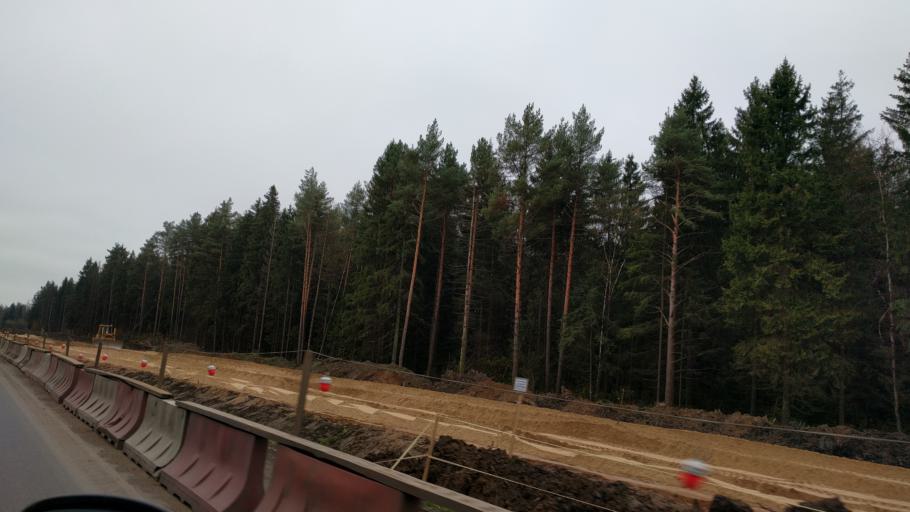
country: RU
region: Moskovskaya
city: Golitsyno
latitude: 55.5840
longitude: 37.0016
